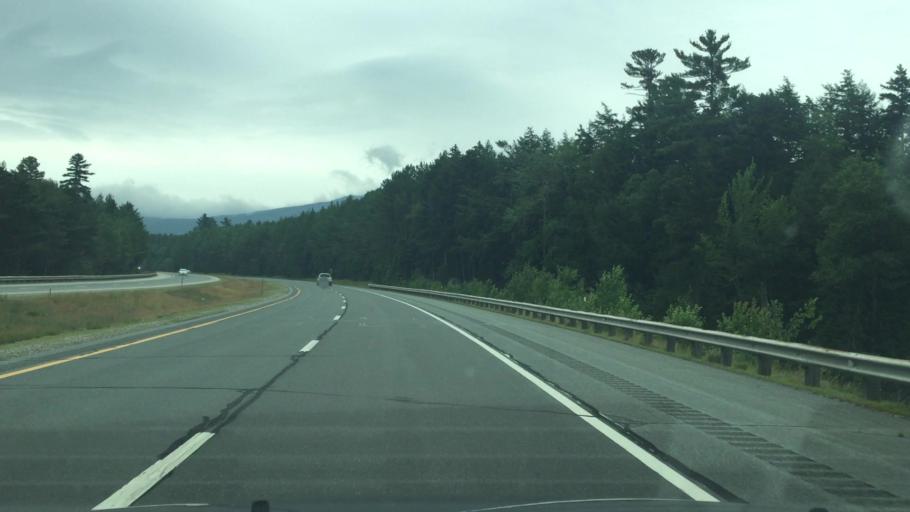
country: US
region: New Hampshire
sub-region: Grafton County
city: Deerfield
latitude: 44.2082
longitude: -71.7200
